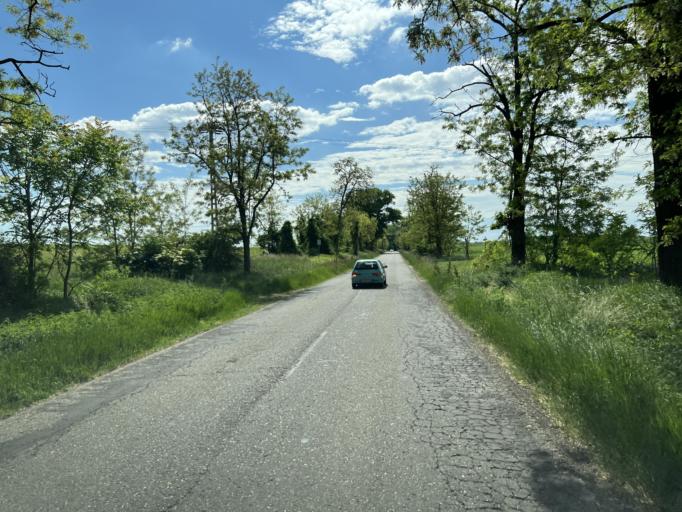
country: HU
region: Pest
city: Vacszentlaszlo
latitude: 47.5564
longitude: 19.5697
